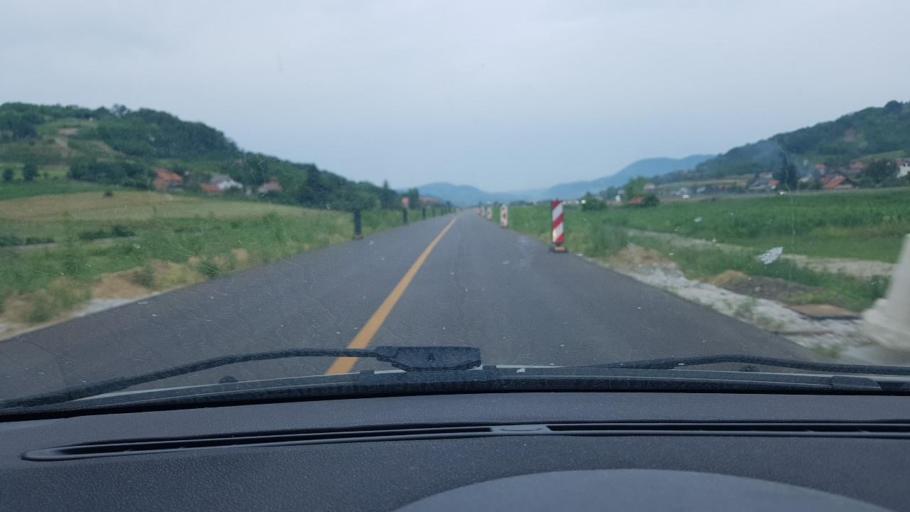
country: HR
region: Krapinsko-Zagorska
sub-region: Grad Krapina
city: Krapina
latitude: 46.0996
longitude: 15.8974
